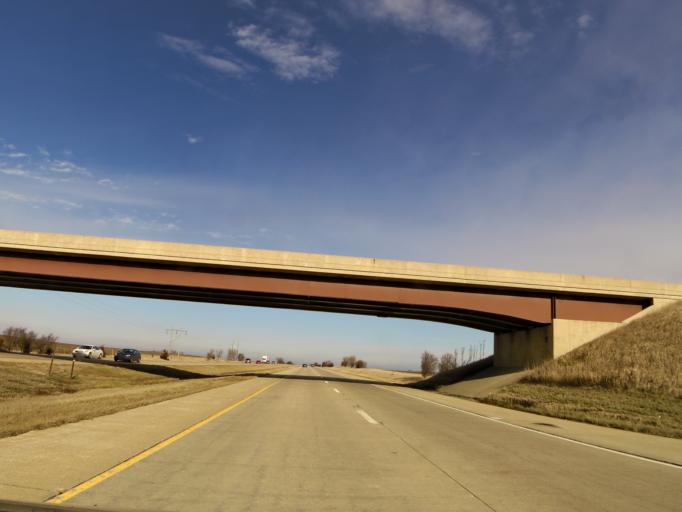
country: US
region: Illinois
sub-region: Marshall County
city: Wenona
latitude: 41.1477
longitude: -89.0755
